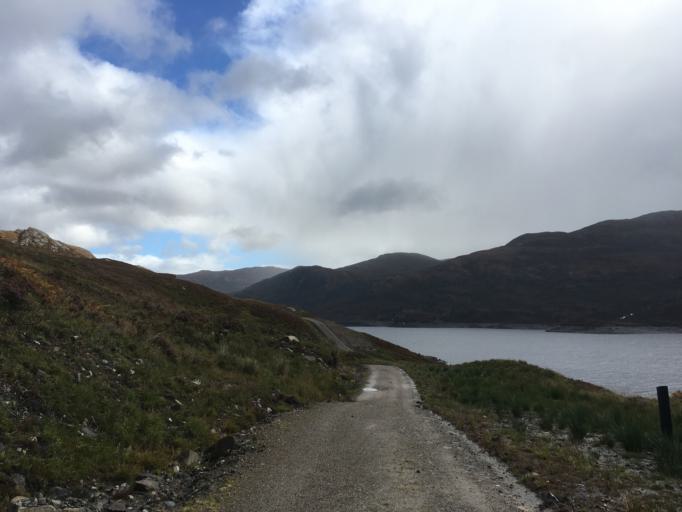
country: GB
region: Scotland
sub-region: Highland
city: Spean Bridge
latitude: 57.3417
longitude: -4.9797
